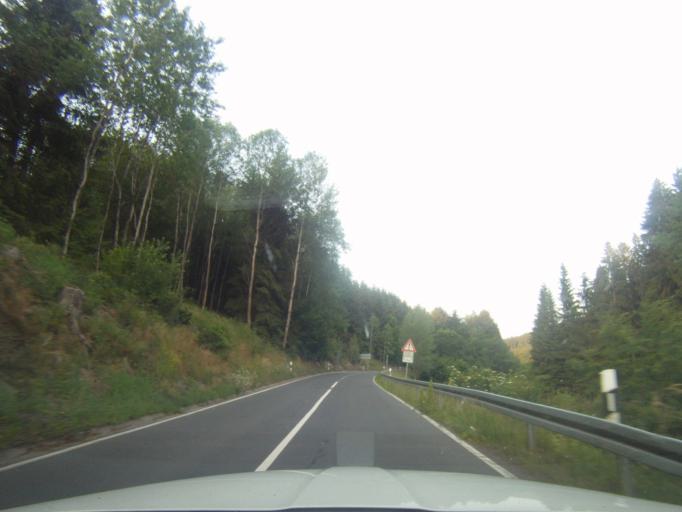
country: DE
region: Thuringia
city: Eisfeld
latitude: 50.4866
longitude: 10.9081
